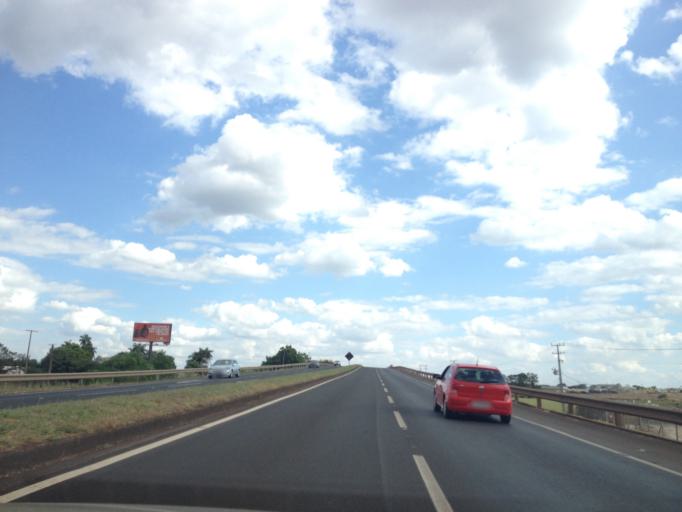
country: BR
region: Parana
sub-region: Marialva
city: Marialva
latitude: -23.4746
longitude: -51.8202
